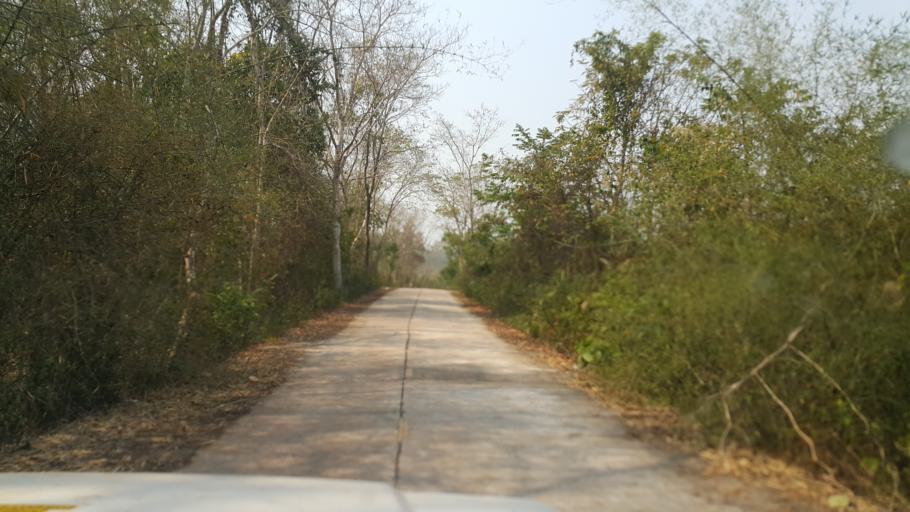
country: TH
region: Nakhon Phanom
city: Ban Phaeng
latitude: 17.9824
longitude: 104.1467
